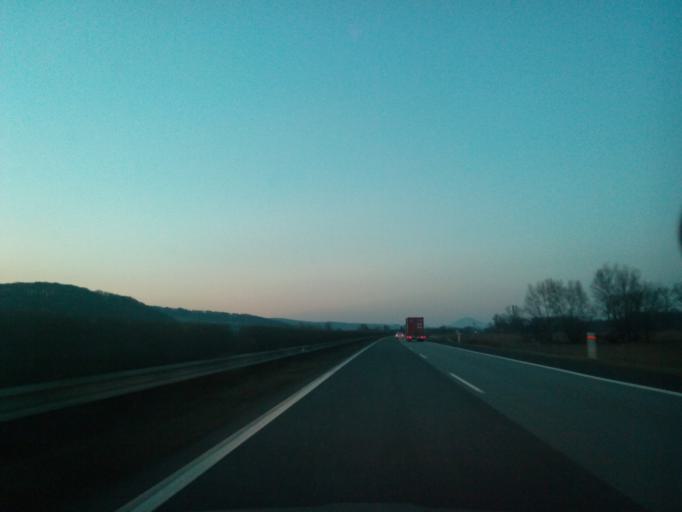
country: SK
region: Presovsky
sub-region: Okres Presov
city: Presov
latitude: 48.8871
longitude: 21.2494
